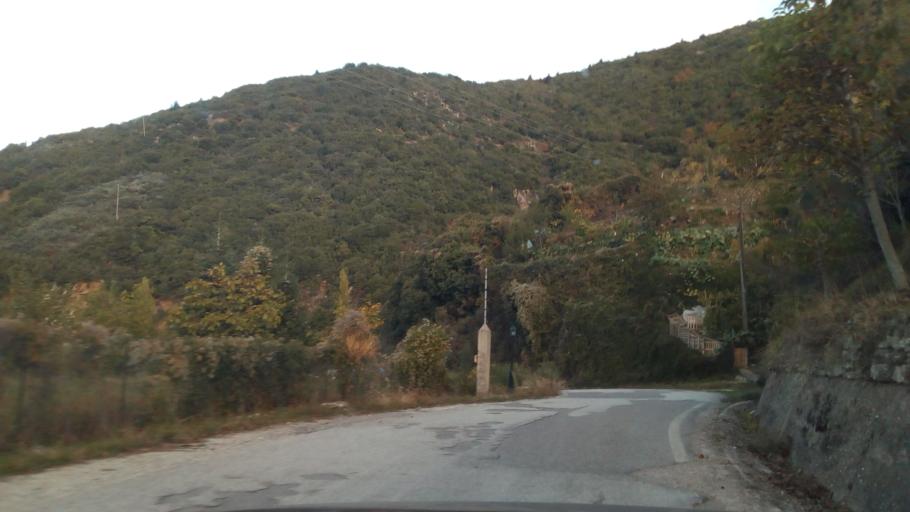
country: GR
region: West Greece
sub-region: Nomos Aitolias kai Akarnanias
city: Nafpaktos
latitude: 38.5324
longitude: 21.8255
